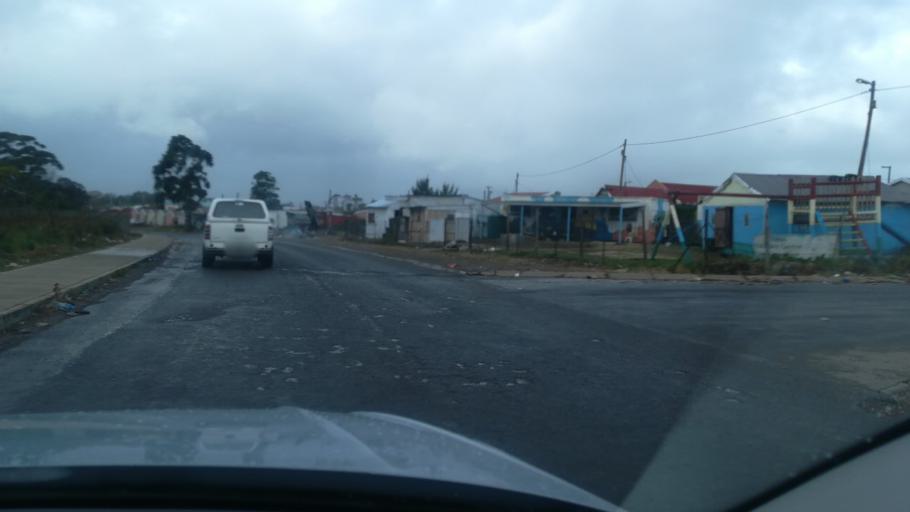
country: ZA
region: Eastern Cape
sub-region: Buffalo City Metropolitan Municipality
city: East London
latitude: -33.0011
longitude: 27.8353
